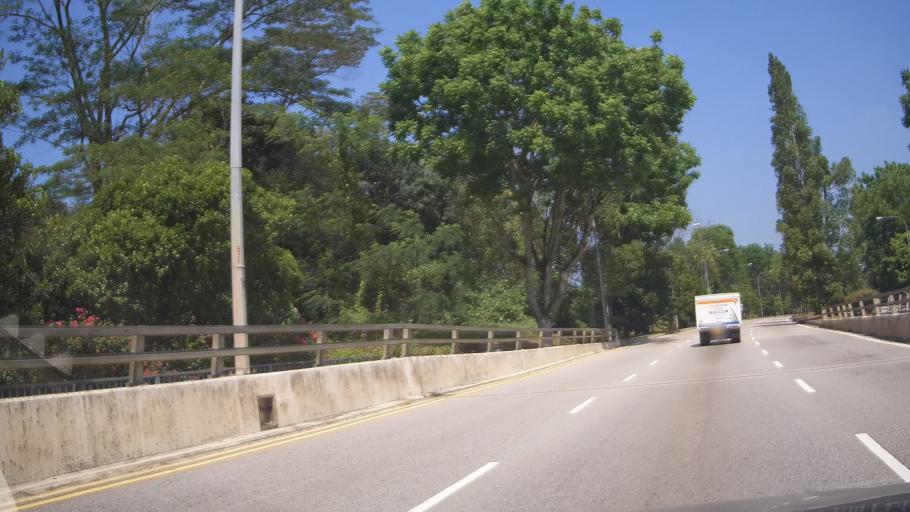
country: MY
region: Johor
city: Johor Bahru
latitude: 1.4167
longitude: 103.7623
